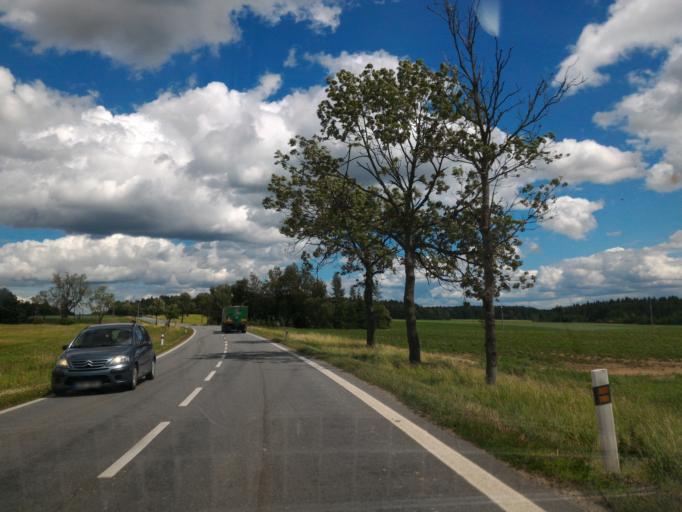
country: CZ
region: Vysocina
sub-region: Okres Zd'ar nad Sazavou
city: Nove Veseli
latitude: 49.5359
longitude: 15.9176
